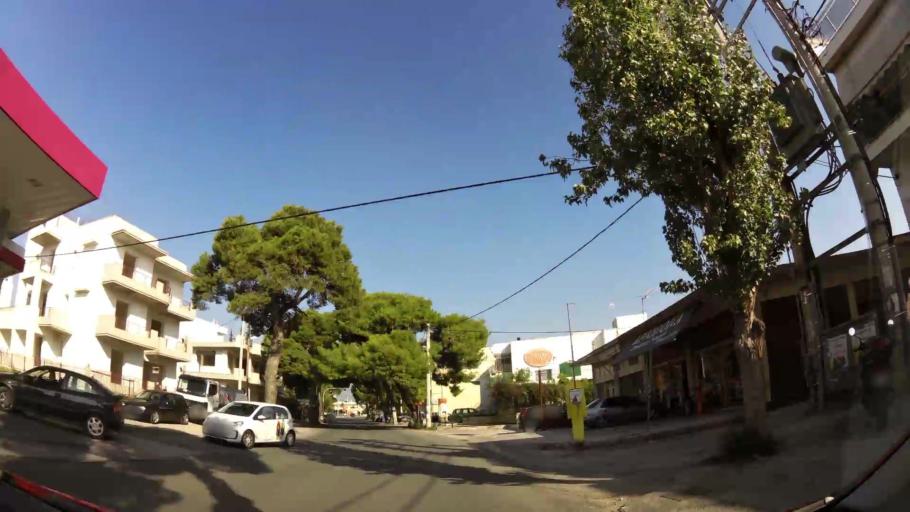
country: GR
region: Attica
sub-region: Nomarchia Anatolikis Attikis
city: Acharnes
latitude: 38.0626
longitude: 23.7393
